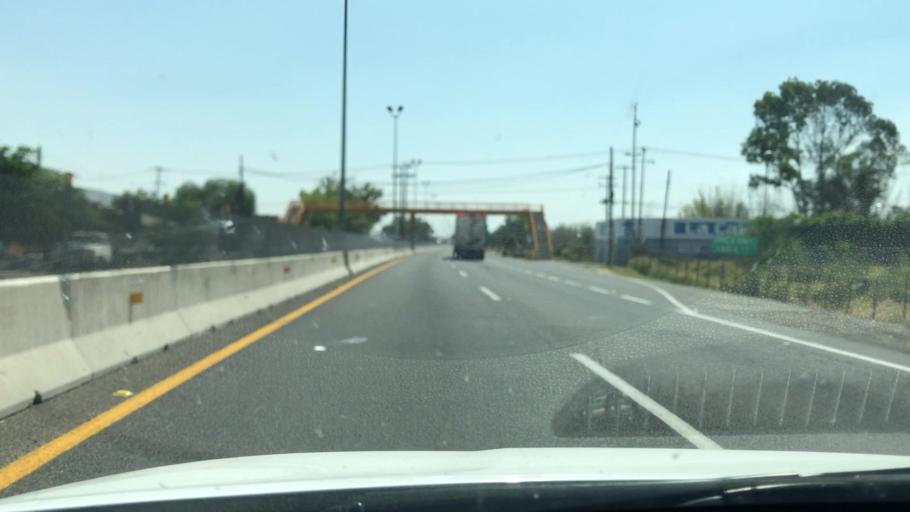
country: MX
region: Guanajuato
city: Abasolo
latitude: 20.4596
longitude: -101.5299
